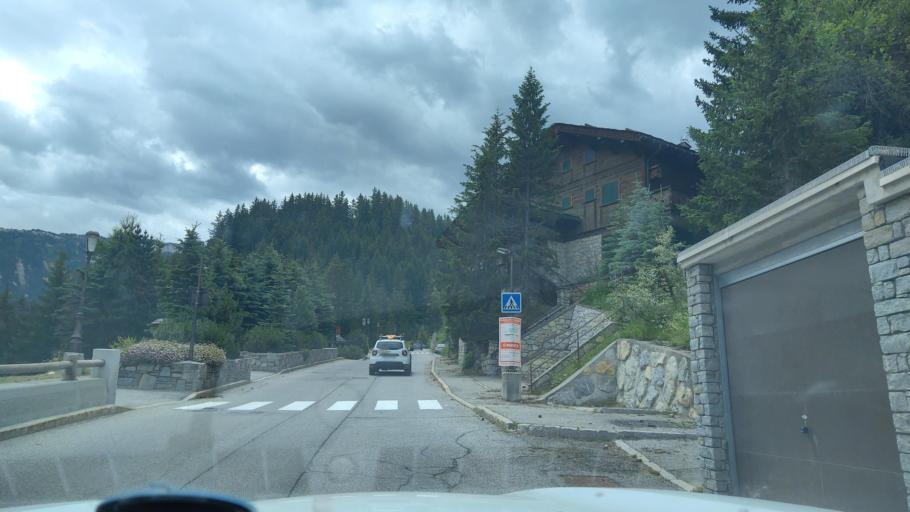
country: FR
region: Rhone-Alpes
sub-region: Departement de la Savoie
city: Courchevel
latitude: 45.4163
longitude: 6.6553
